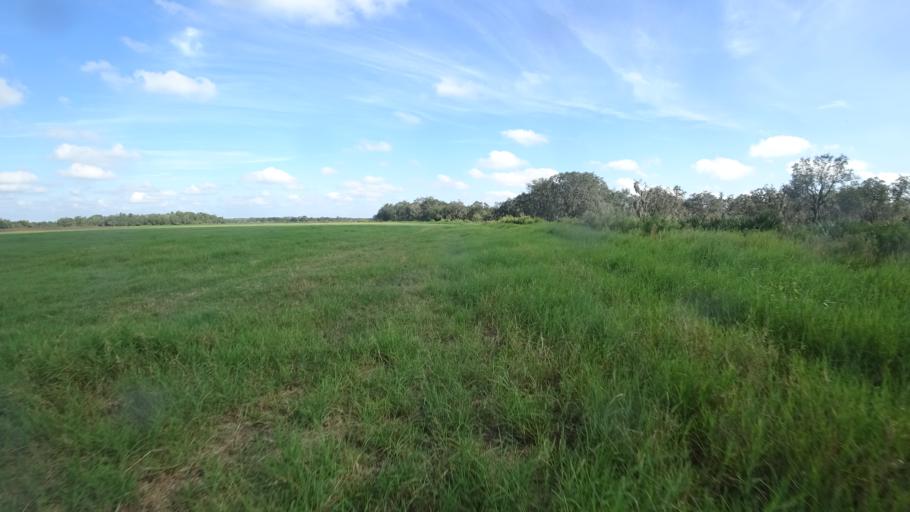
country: US
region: Florida
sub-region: Sarasota County
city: Lake Sarasota
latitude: 27.3727
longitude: -82.1652
